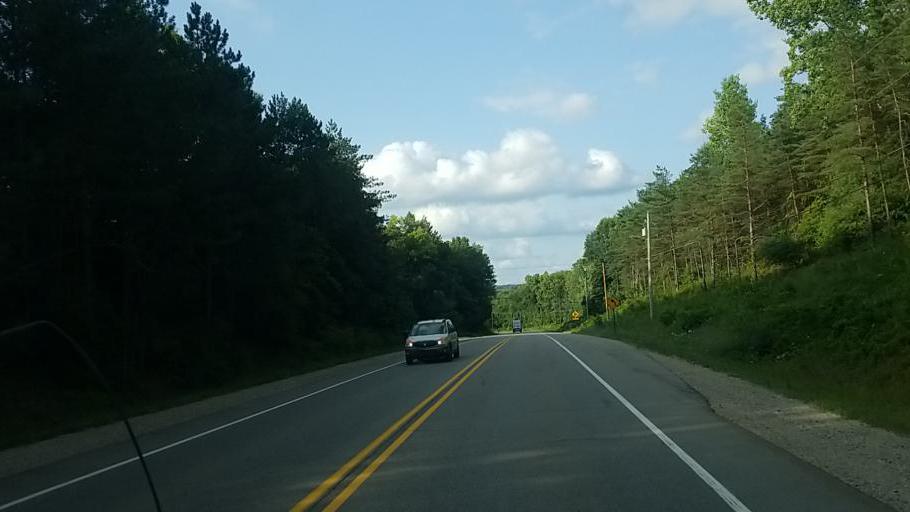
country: US
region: Michigan
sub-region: Kent County
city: Lowell
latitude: 42.9168
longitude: -85.3452
